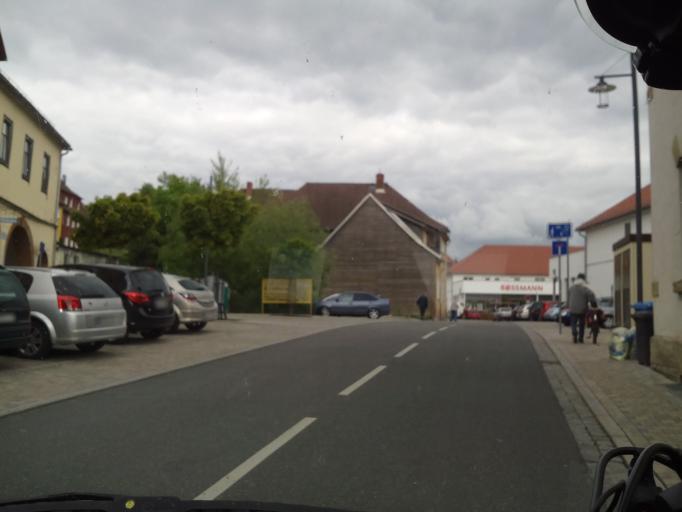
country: DE
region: Thuringia
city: Hildburghausen
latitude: 50.4259
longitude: 10.7265
